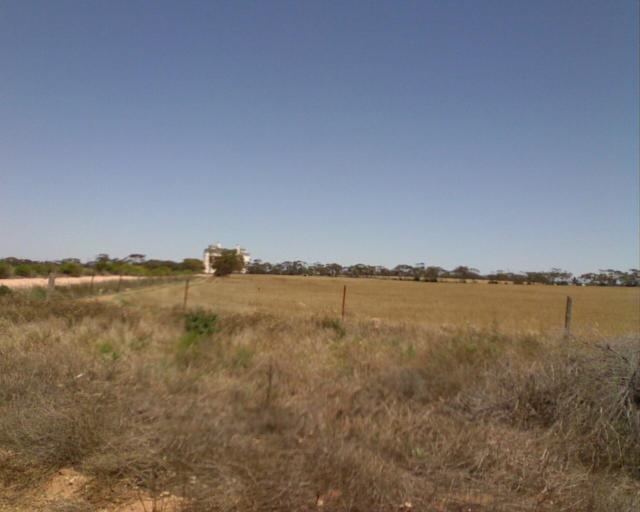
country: AU
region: South Australia
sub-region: Kimba
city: Caralue
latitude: -32.9481
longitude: 135.2831
